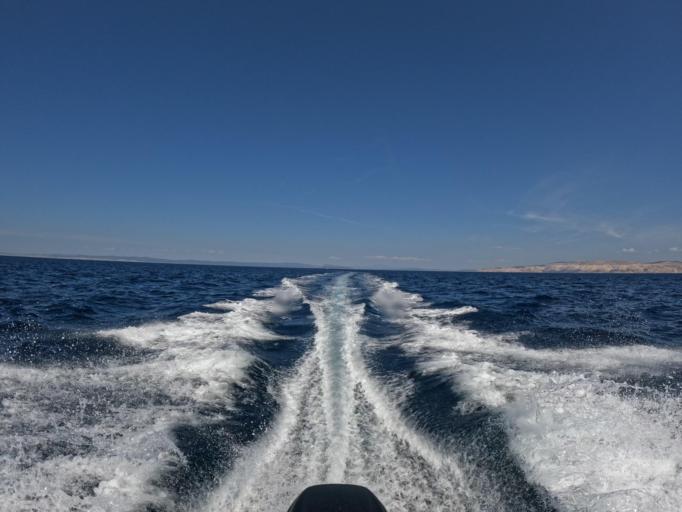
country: HR
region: Primorsko-Goranska
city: Lopar
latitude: 44.8584
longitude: 14.6949
